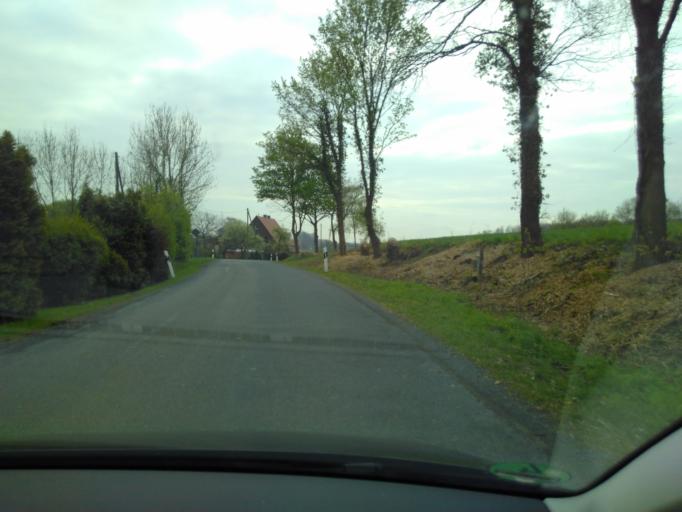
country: DE
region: North Rhine-Westphalia
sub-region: Regierungsbezirk Munster
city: Beckum
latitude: 51.7679
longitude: 8.1032
